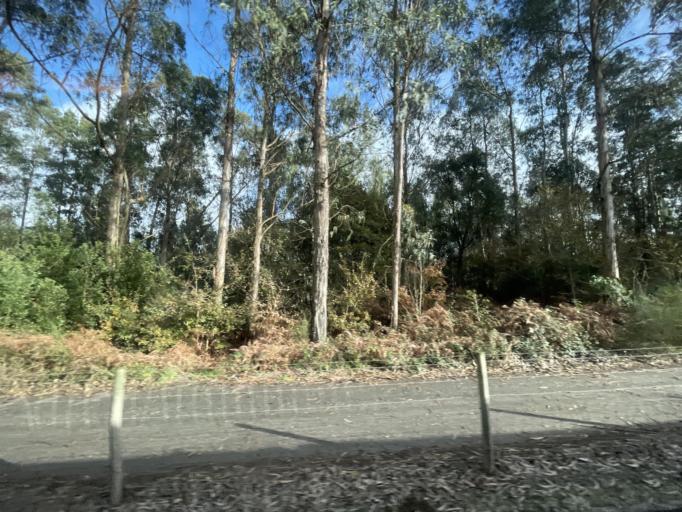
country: PT
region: Porto
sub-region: Vila do Conde
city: Arvore
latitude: 41.3473
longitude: -8.7281
